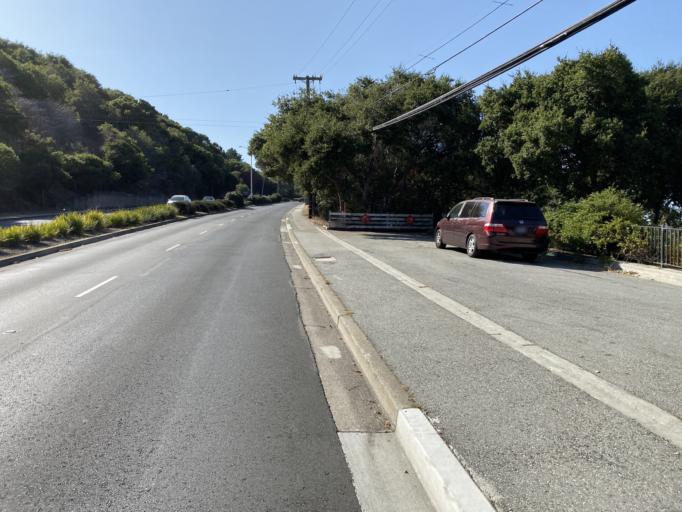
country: US
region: California
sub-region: San Mateo County
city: Belmont
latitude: 37.5125
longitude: -122.3057
